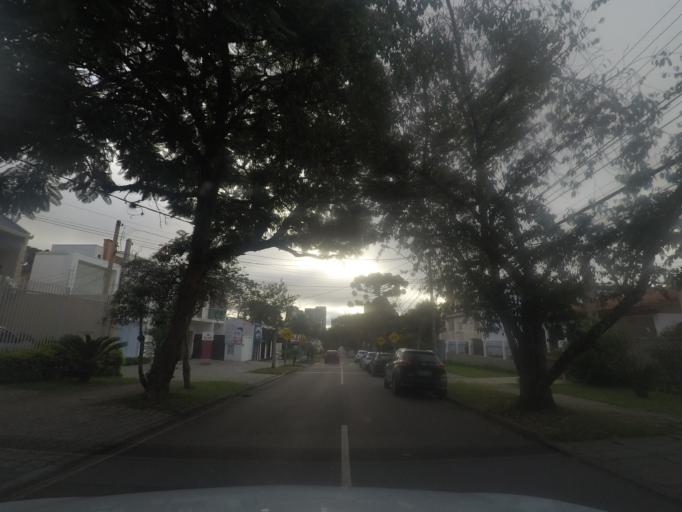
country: BR
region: Parana
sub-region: Curitiba
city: Curitiba
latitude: -25.4305
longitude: -49.2444
